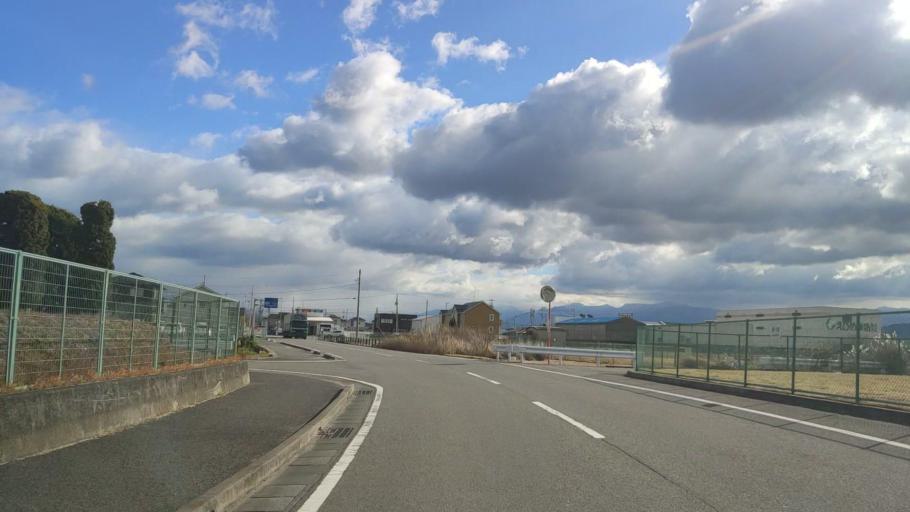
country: JP
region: Ehime
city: Masaki-cho
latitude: 33.8223
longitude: 132.7109
